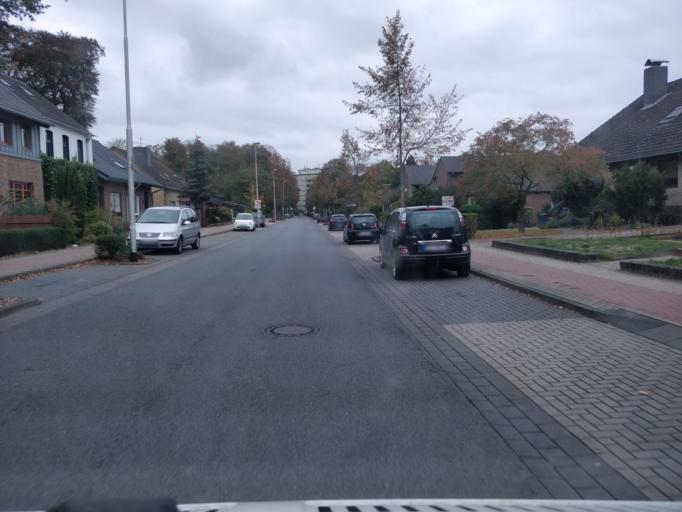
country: DE
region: North Rhine-Westphalia
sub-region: Regierungsbezirk Dusseldorf
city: Emmerich
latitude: 51.8463
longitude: 6.2421
